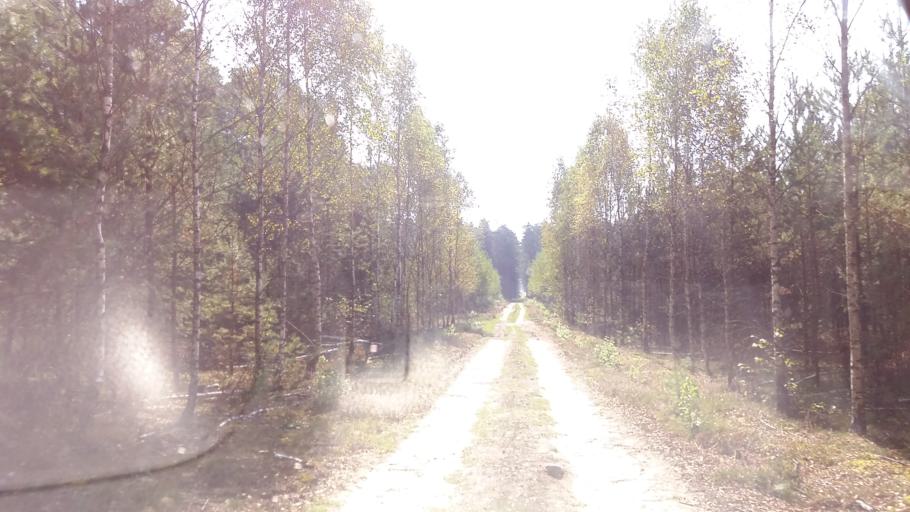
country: PL
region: West Pomeranian Voivodeship
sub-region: Powiat drawski
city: Kalisz Pomorski
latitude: 53.1935
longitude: 15.8964
